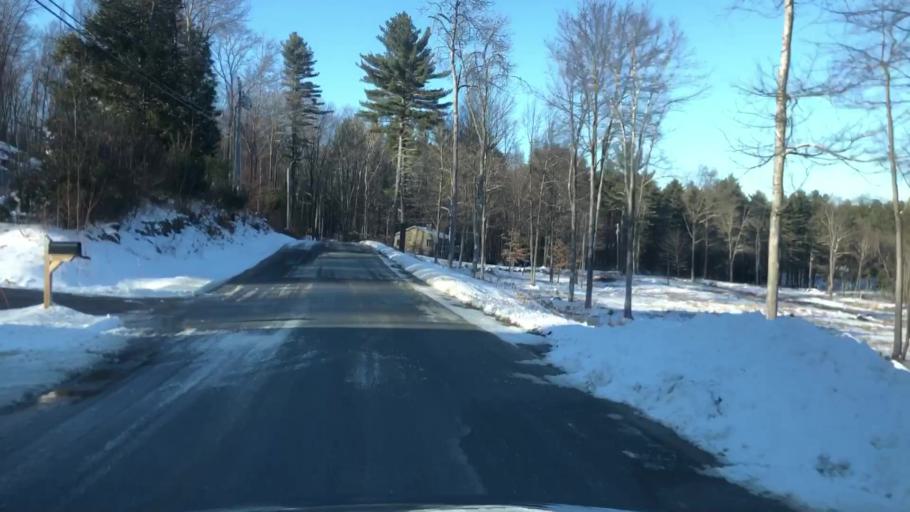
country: US
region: New Hampshire
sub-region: Hillsborough County
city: Wilton
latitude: 42.8052
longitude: -71.7067
